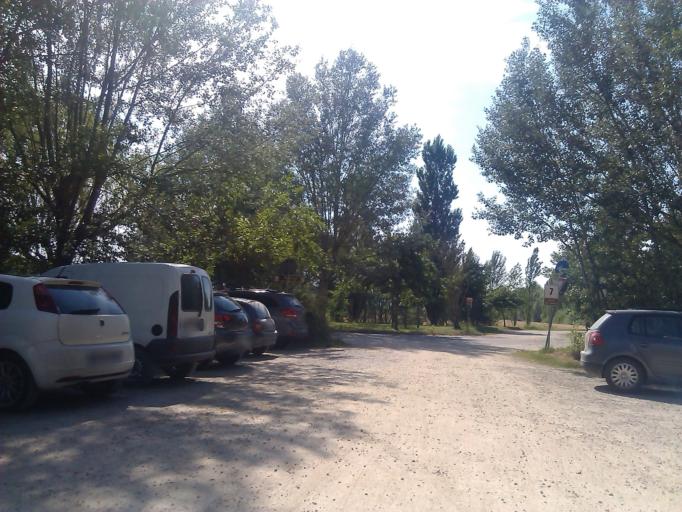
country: IT
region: Tuscany
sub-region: Provincia di Siena
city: Chiusi
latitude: 43.0506
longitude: 11.9573
